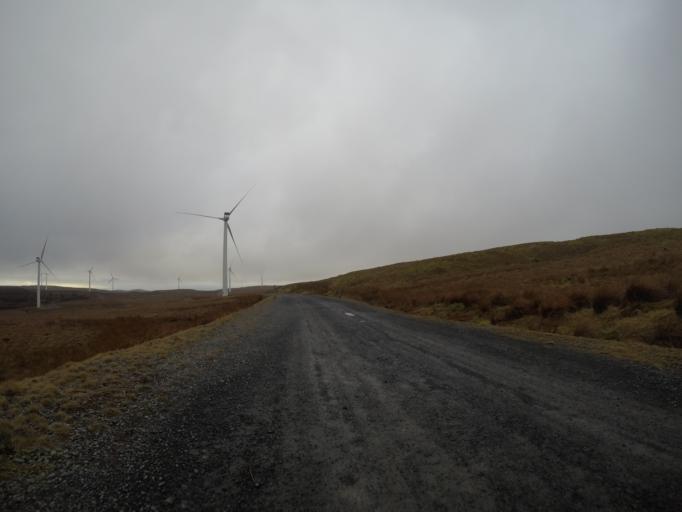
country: GB
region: Scotland
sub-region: North Ayrshire
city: Fairlie
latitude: 55.7594
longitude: -4.7932
